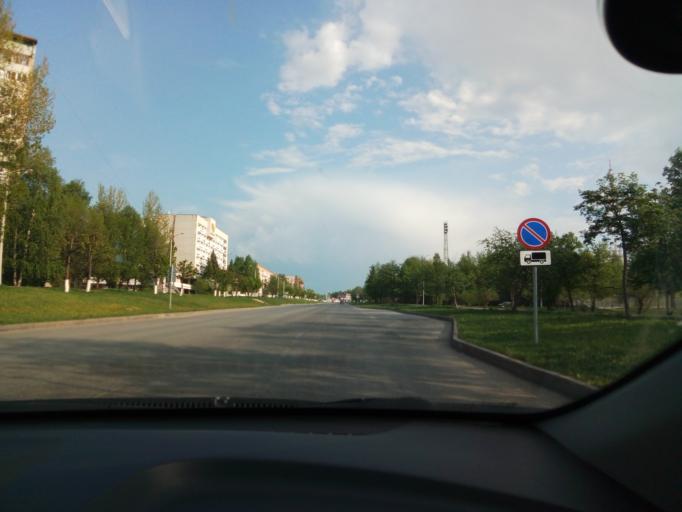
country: RU
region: Chuvashia
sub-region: Cheboksarskiy Rayon
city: Cheboksary
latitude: 56.1260
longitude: 47.2678
